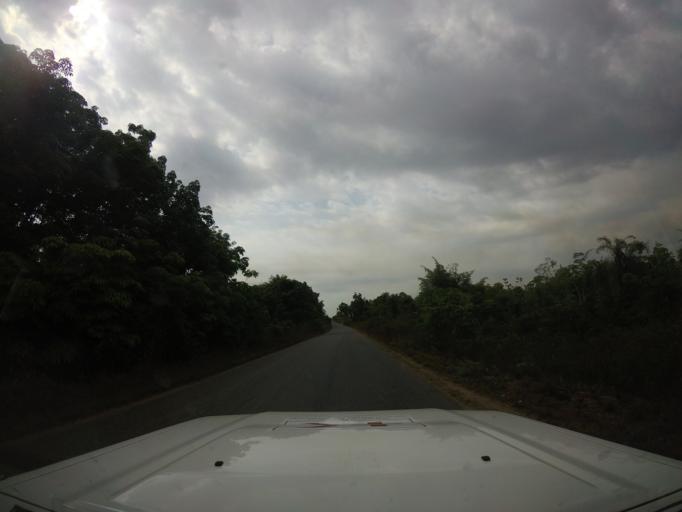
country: LR
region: Montserrado
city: Monrovia
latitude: 6.5573
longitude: -10.8679
